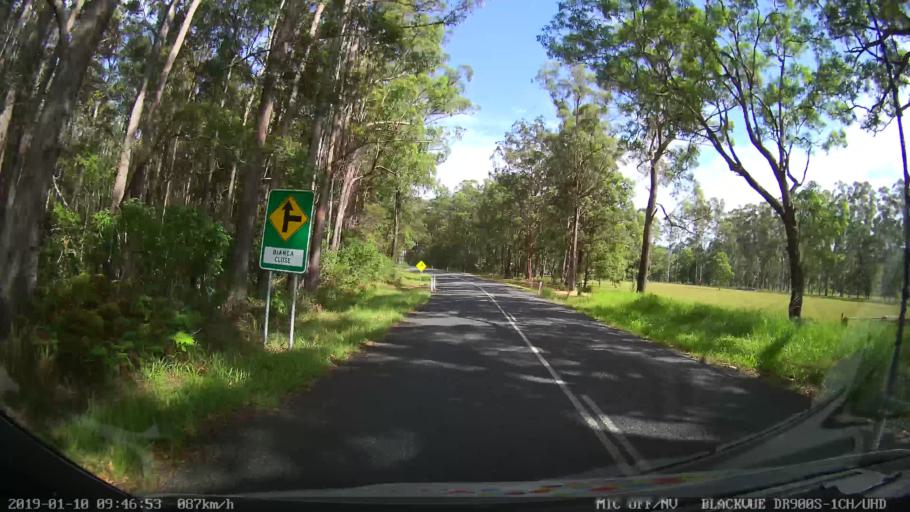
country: AU
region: New South Wales
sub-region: Coffs Harbour
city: Nana Glen
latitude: -30.0874
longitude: 153.0019
